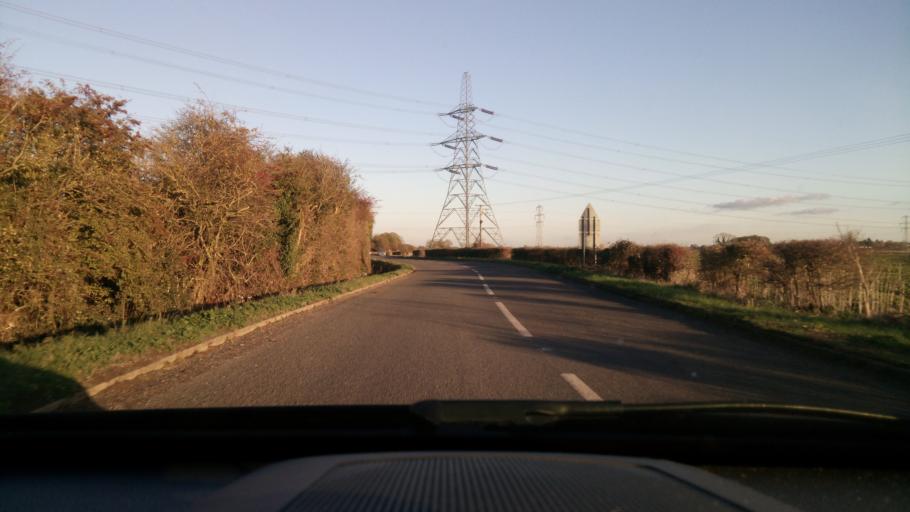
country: GB
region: England
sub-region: Peterborough
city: Helpston
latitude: 52.6434
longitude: -0.3686
